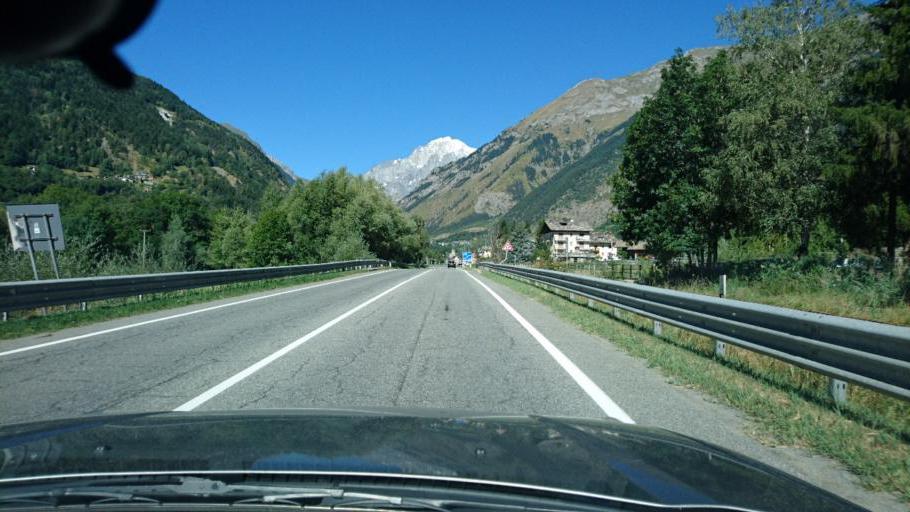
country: IT
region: Aosta Valley
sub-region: Valle d'Aosta
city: Morgex
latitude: 45.7525
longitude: 7.0465
